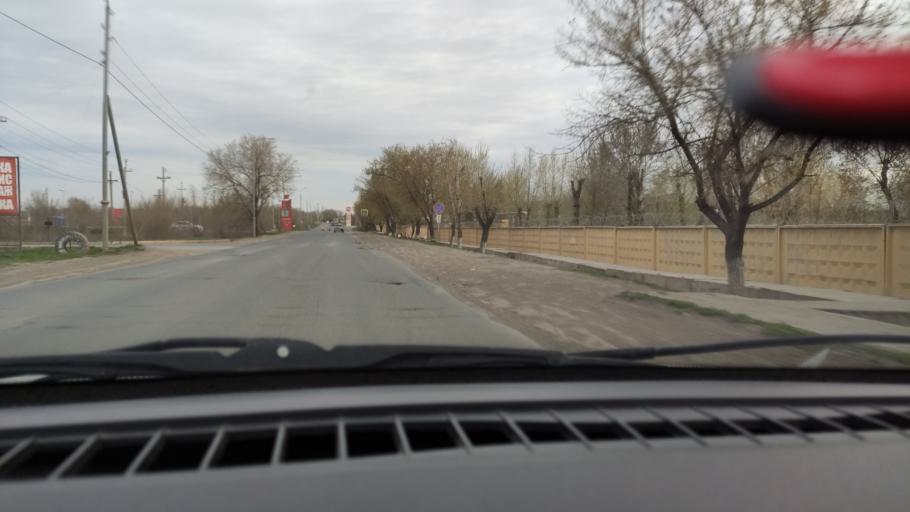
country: RU
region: Orenburg
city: Tatarskaya Kargala
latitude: 51.8813
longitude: 55.1510
